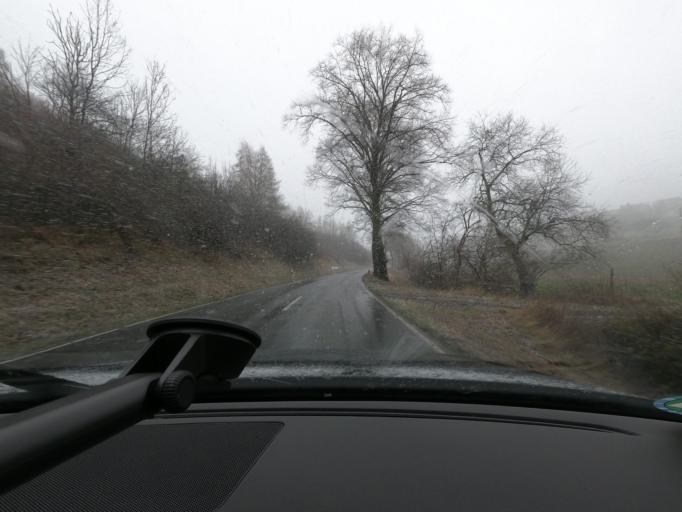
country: DE
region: North Rhine-Westphalia
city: Marsberg
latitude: 51.5045
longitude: 8.9036
